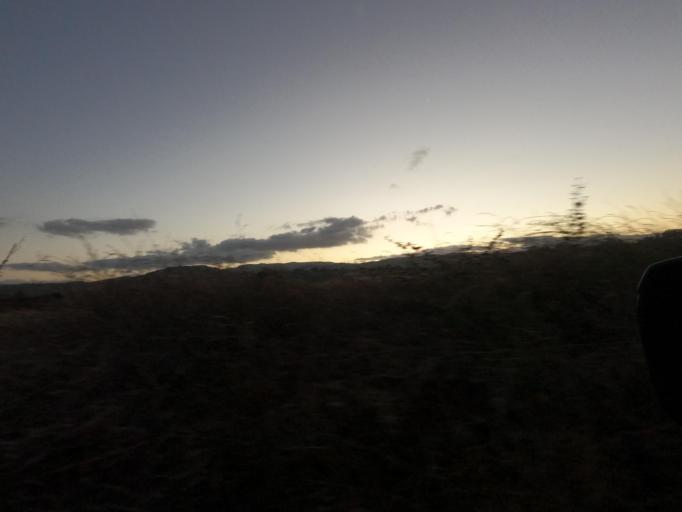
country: CY
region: Pafos
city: Mesogi
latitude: 34.8534
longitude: 32.5424
